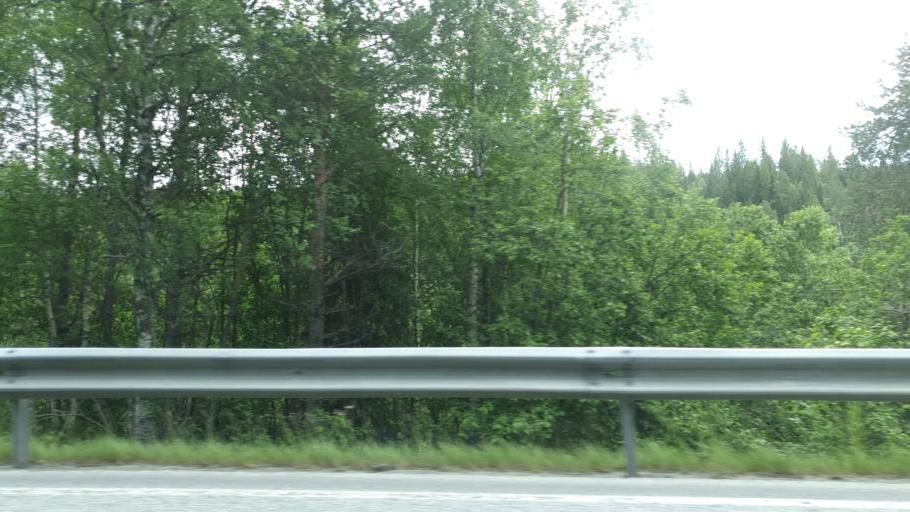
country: NO
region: Sor-Trondelag
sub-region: Rennebu
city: Berkak
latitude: 62.8693
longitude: 10.0819
